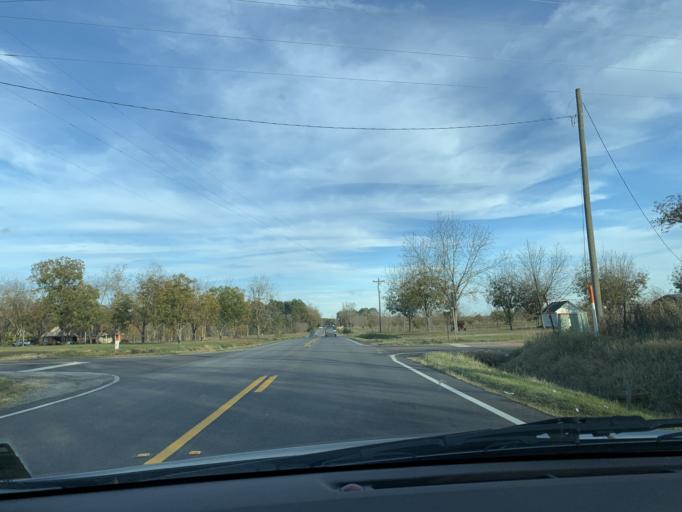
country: US
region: Georgia
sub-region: Irwin County
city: Ocilla
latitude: 31.5927
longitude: -83.2187
